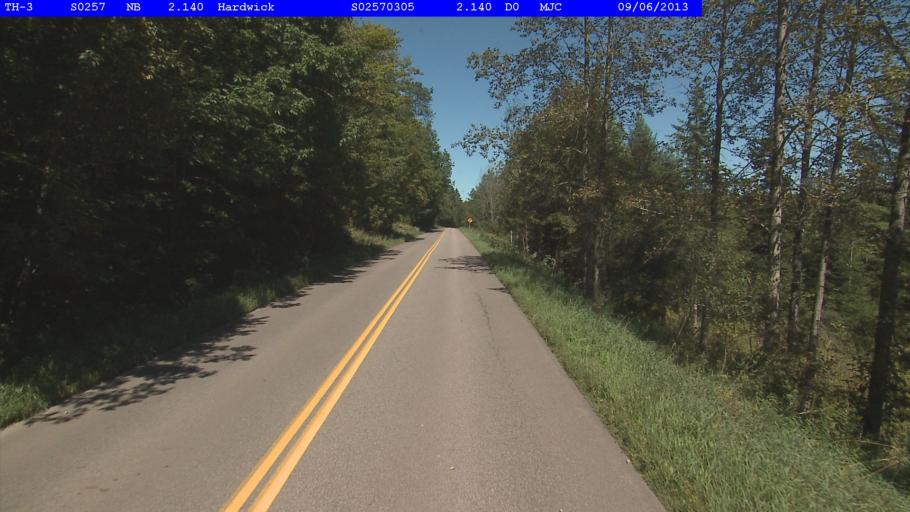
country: US
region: Vermont
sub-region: Caledonia County
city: Hardwick
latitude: 44.5219
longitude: -72.3407
